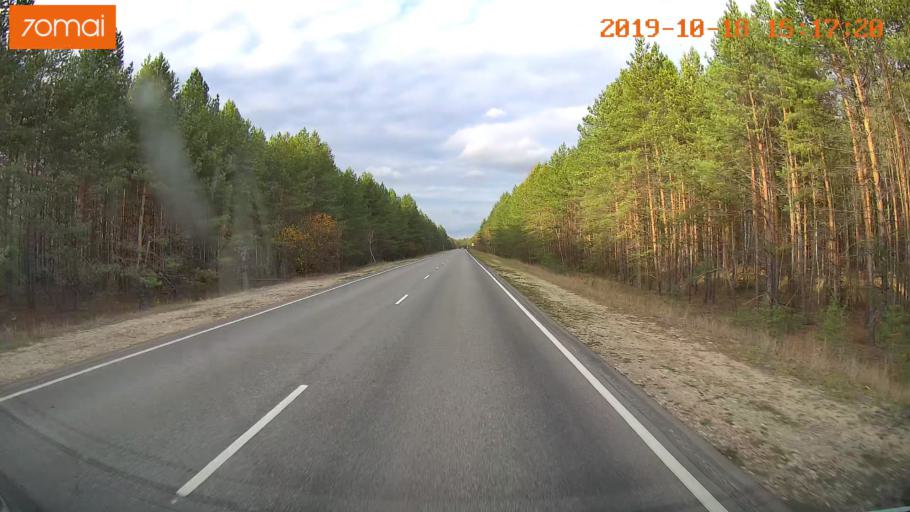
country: RU
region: Vladimir
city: Anopino
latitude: 55.6481
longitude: 40.7263
